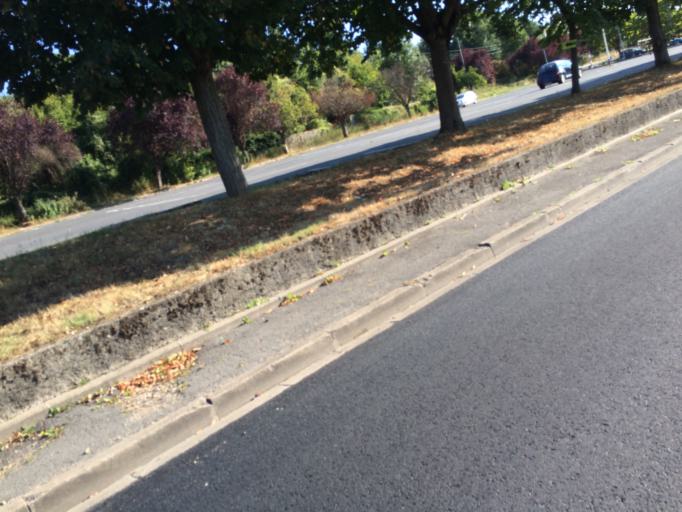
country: FR
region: Ile-de-France
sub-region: Departement de l'Essonne
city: Sainte-Genevieve-des-Bois
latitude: 48.6558
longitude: 2.3161
